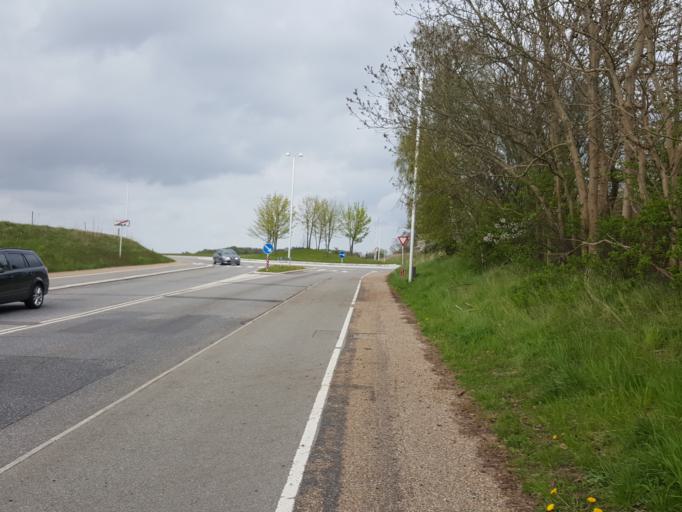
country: DK
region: Capital Region
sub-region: Rudersdal Kommune
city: Birkerod
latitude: 55.8548
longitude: 12.4543
